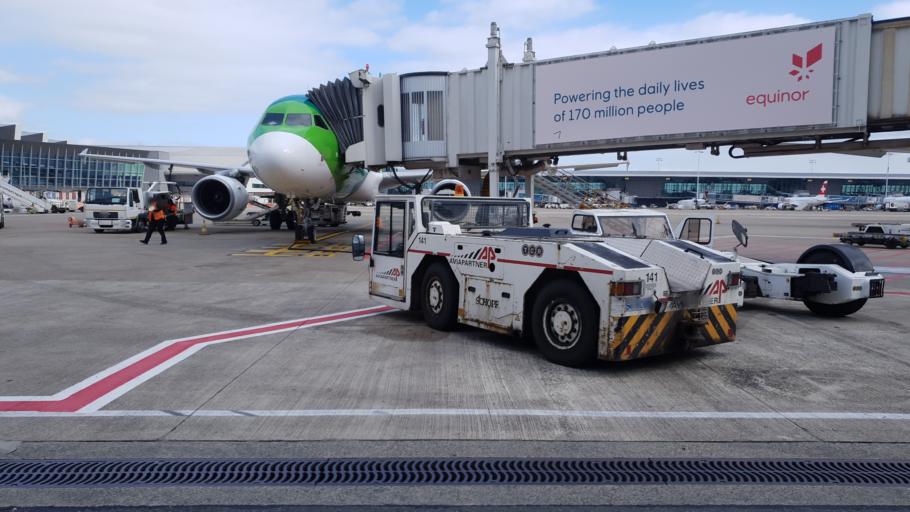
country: BE
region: Flanders
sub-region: Provincie Vlaams-Brabant
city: Zaventem
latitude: 50.8997
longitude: 4.4850
